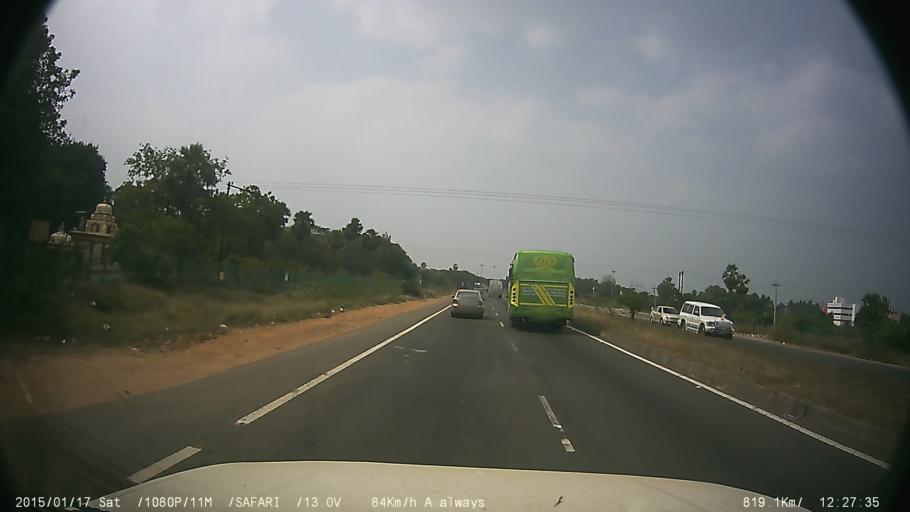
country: IN
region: Tamil Nadu
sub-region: Kancheepuram
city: Kanchipuram
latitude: 12.8712
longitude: 79.7124
